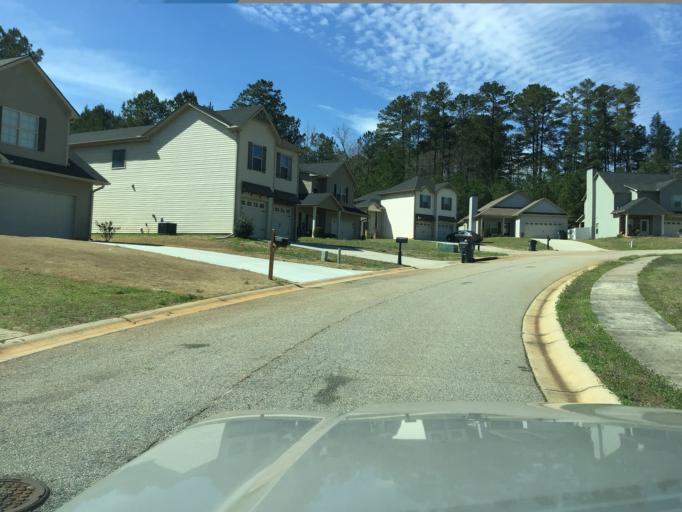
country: US
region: Georgia
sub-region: Coweta County
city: Grantville
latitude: 33.2351
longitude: -84.8242
